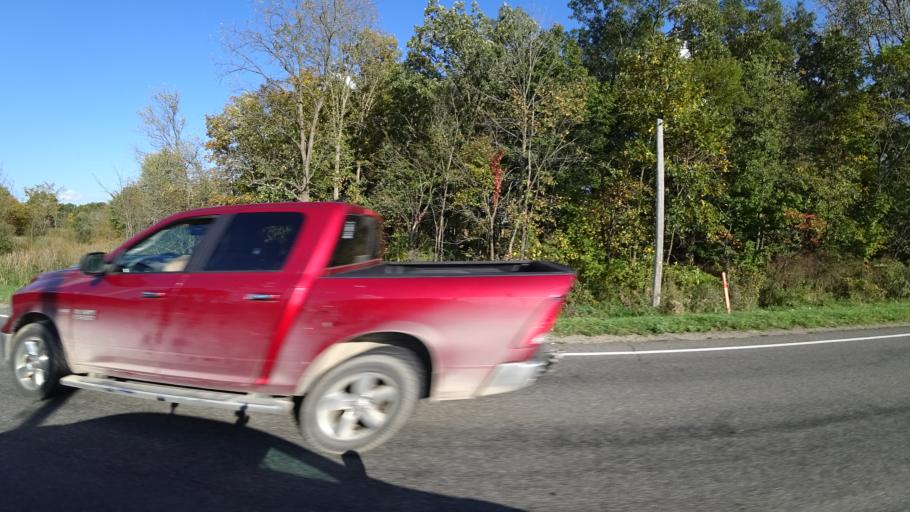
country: US
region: Michigan
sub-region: Saint Joseph County
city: Centreville
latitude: 41.9079
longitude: -85.5070
